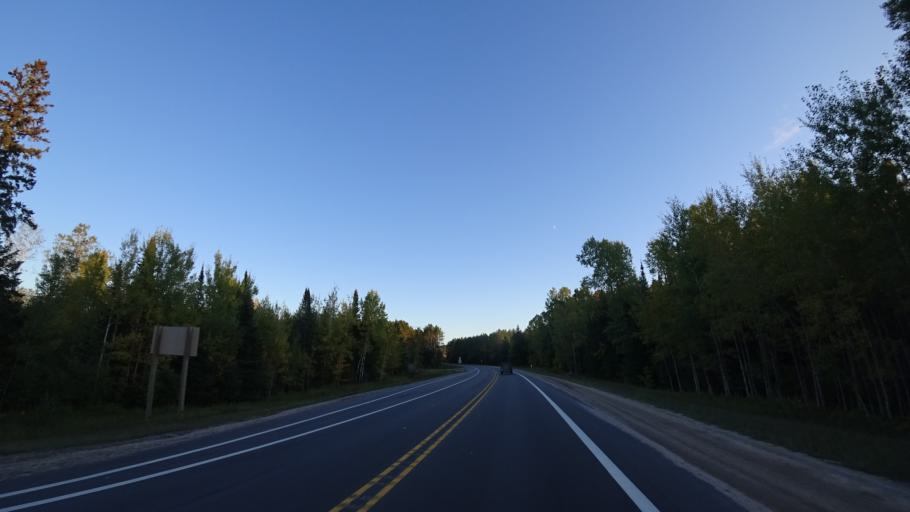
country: US
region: Michigan
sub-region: Luce County
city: Newberry
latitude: 46.3444
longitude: -85.0308
